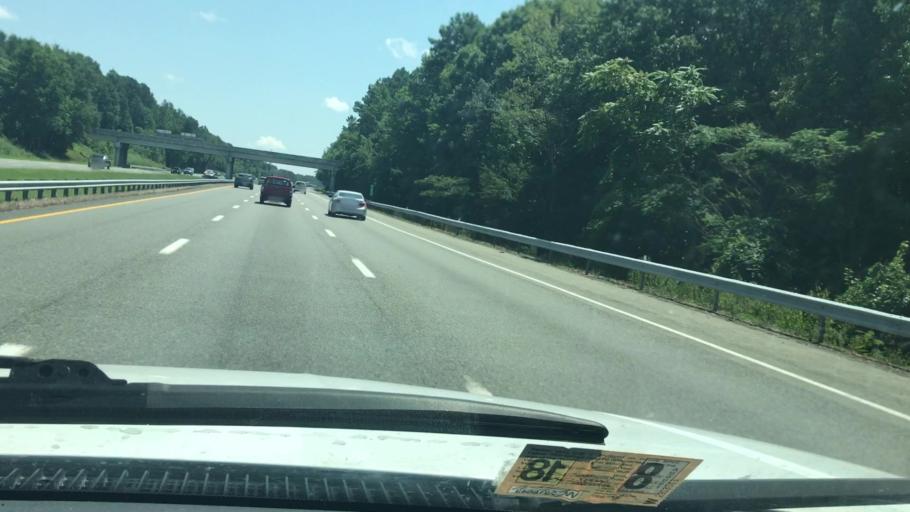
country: US
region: Virginia
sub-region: Henrico County
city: Montrose
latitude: 37.5399
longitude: -77.3880
